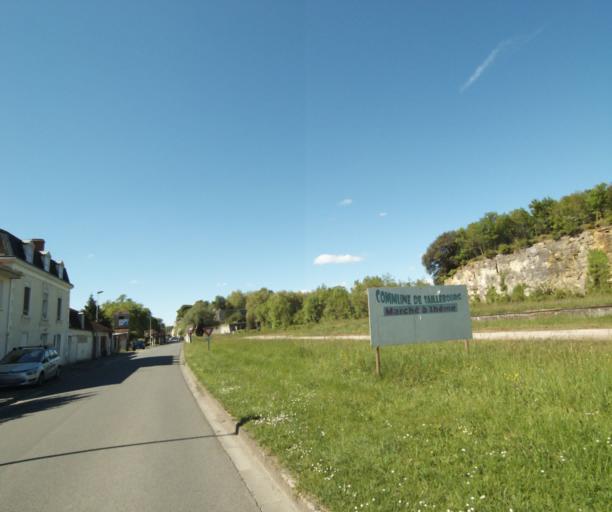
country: FR
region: Poitou-Charentes
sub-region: Departement de la Charente-Maritime
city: Bussac-sur-Charente
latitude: 45.8309
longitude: -0.6458
